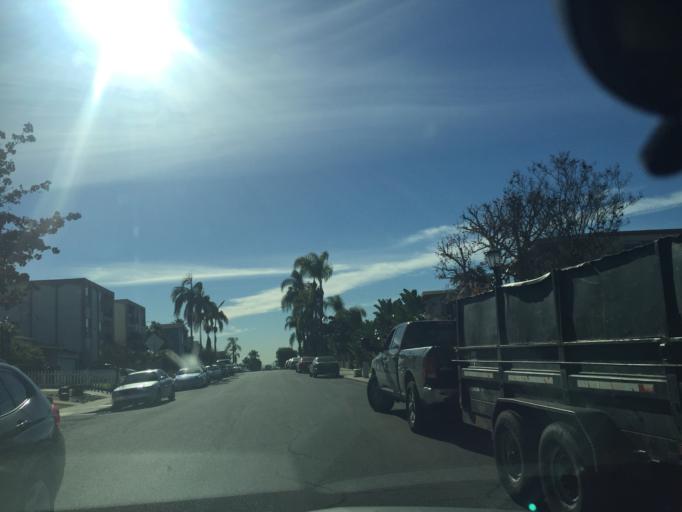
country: US
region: California
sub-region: San Diego County
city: Lemon Grove
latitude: 32.7589
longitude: -117.0890
